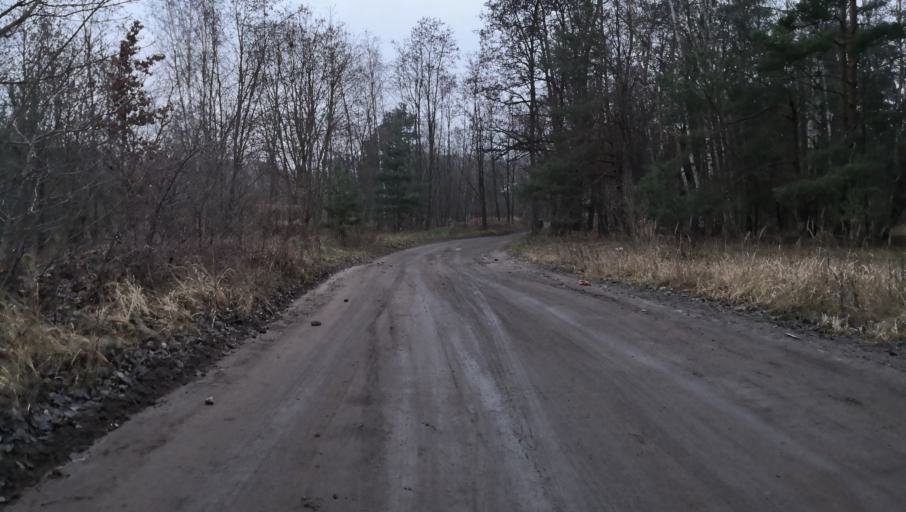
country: PL
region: Lubusz
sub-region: Zielona Gora
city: Zielona Gora
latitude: 51.9496
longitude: 15.4555
